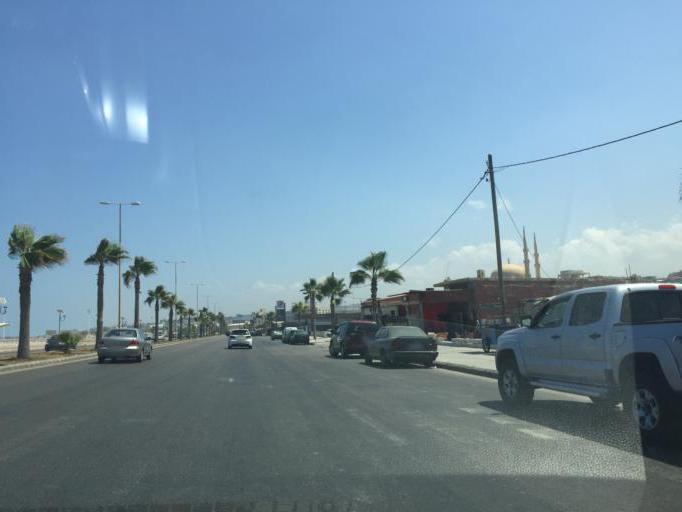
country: LB
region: Liban-Sud
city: Sidon
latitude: 33.5763
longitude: 35.3819
